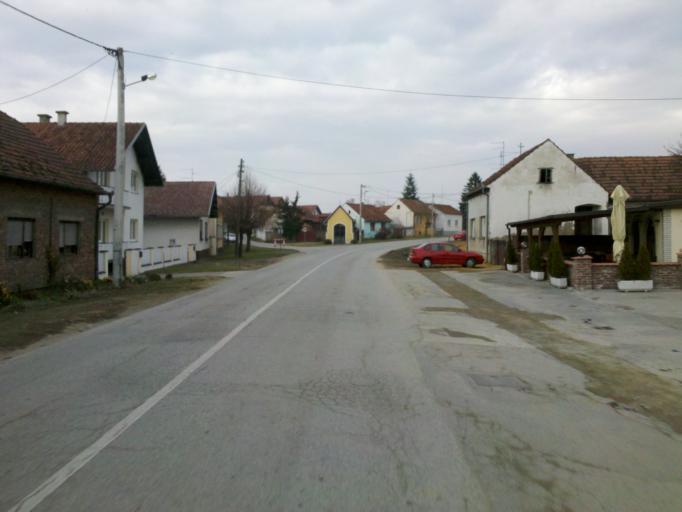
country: HR
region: Koprivnicko-Krizevacka
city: Kalinovac
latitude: 46.0368
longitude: 17.0597
